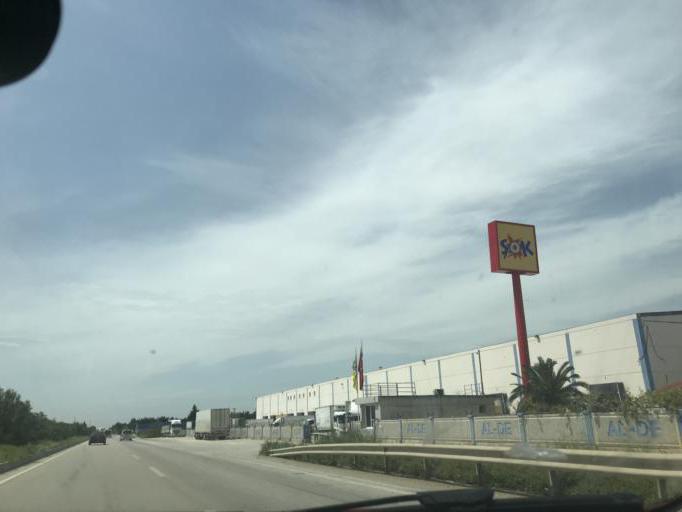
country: TR
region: Adana
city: Yakapinar
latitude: 36.9706
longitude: 35.5279
